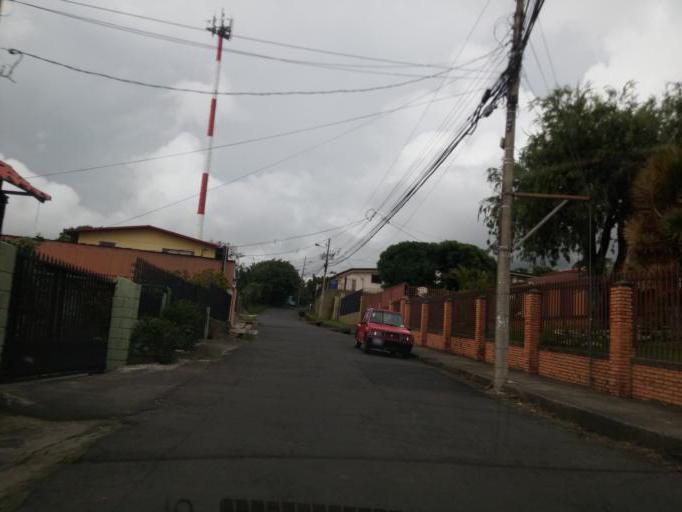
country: CR
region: Heredia
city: Santo Domingo
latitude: 10.0412
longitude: -84.1318
